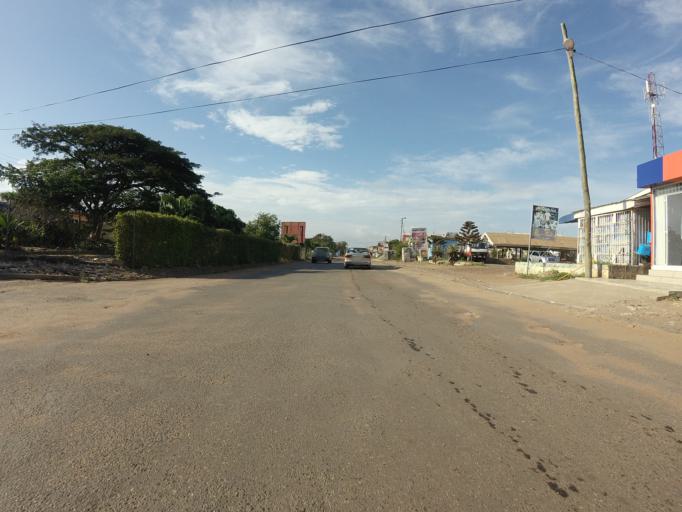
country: GH
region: Greater Accra
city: Tema
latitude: 5.6510
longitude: -0.0643
